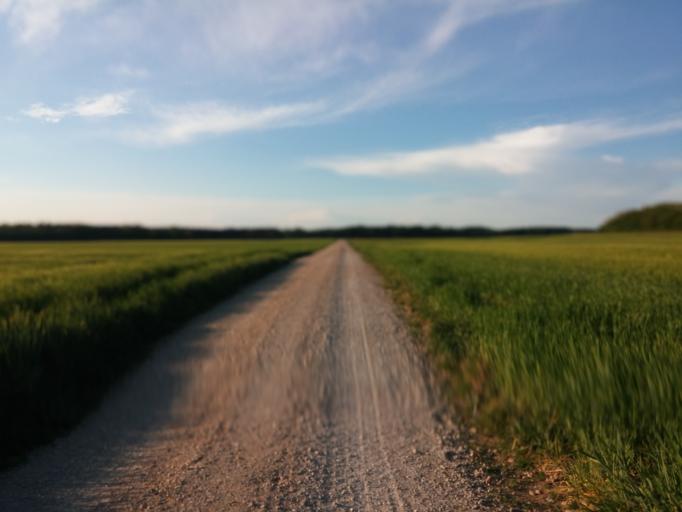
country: DE
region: Bavaria
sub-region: Upper Bavaria
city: Zorneding
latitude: 48.1022
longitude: 11.8182
